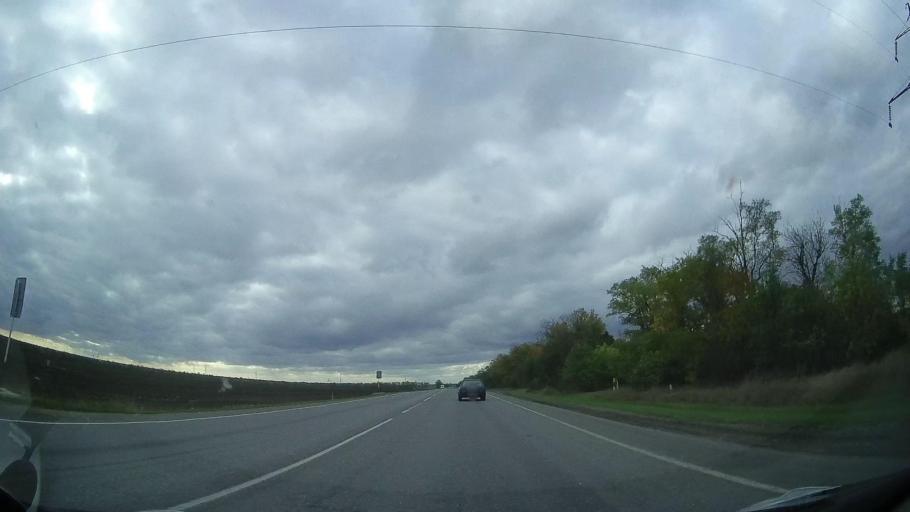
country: RU
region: Rostov
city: Zernograd
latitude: 46.8143
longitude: 40.2817
